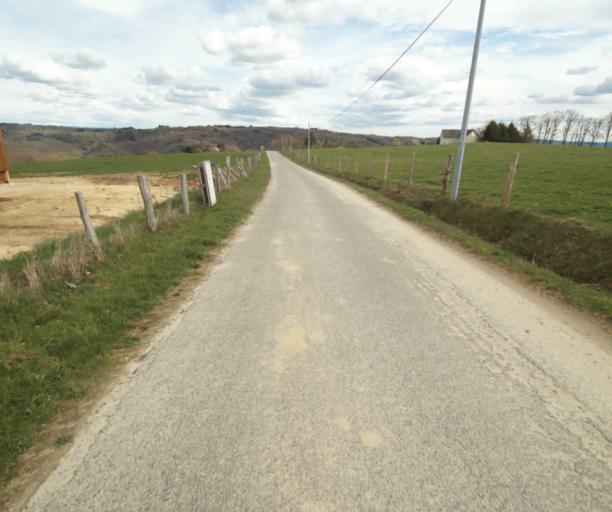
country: FR
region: Limousin
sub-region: Departement de la Correze
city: Argentat
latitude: 45.1818
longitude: 1.9423
